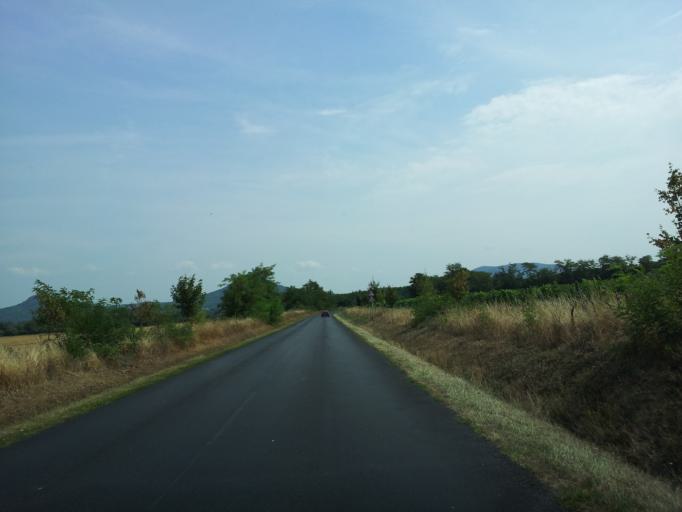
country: HU
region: Veszprem
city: Tapolca
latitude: 46.8557
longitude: 17.4597
